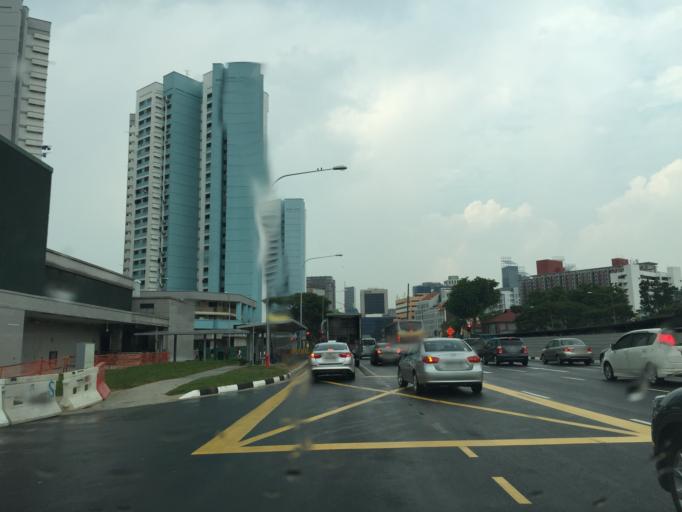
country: SG
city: Singapore
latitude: 1.3067
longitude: 103.8490
